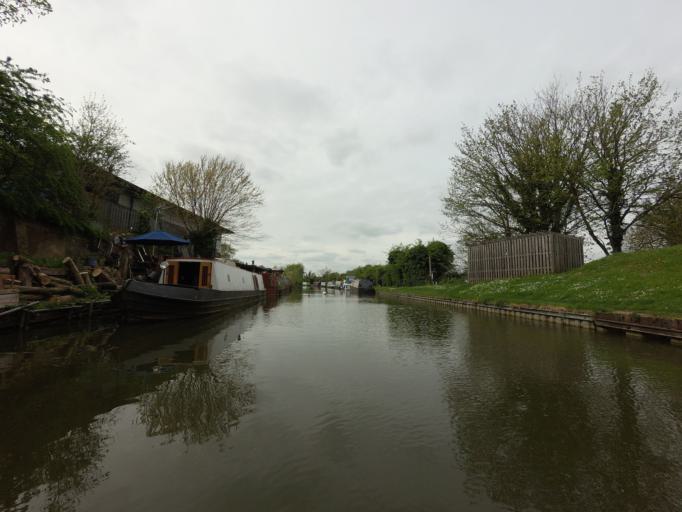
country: GB
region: England
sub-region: Milton Keynes
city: Bradwell
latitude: 52.0732
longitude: -0.7677
